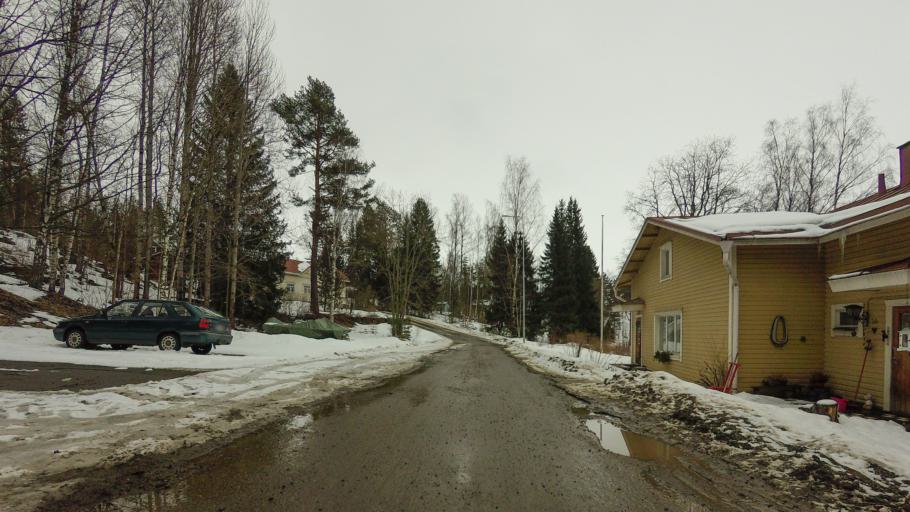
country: FI
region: Southern Savonia
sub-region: Savonlinna
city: Rantasalmi
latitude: 62.1134
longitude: 28.6078
